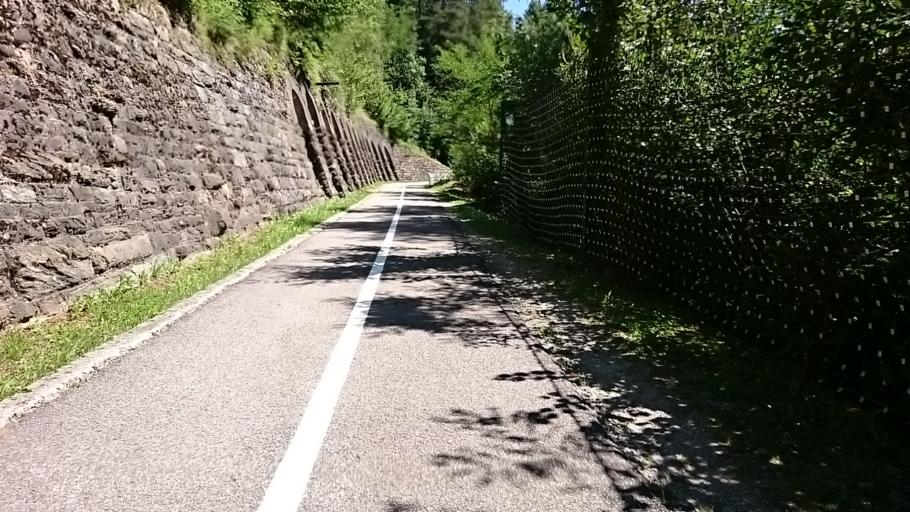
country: IT
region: Veneto
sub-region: Provincia di Belluno
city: Valle di Cadore
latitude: 46.4168
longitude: 12.3186
